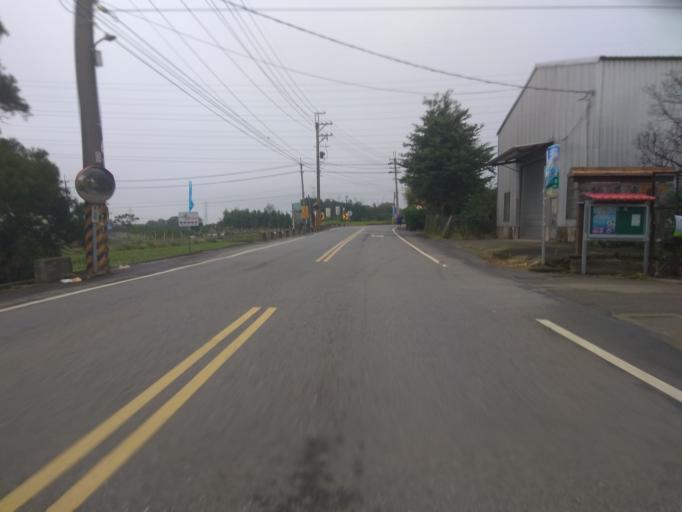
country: TW
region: Taiwan
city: Taoyuan City
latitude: 24.9914
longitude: 121.1255
